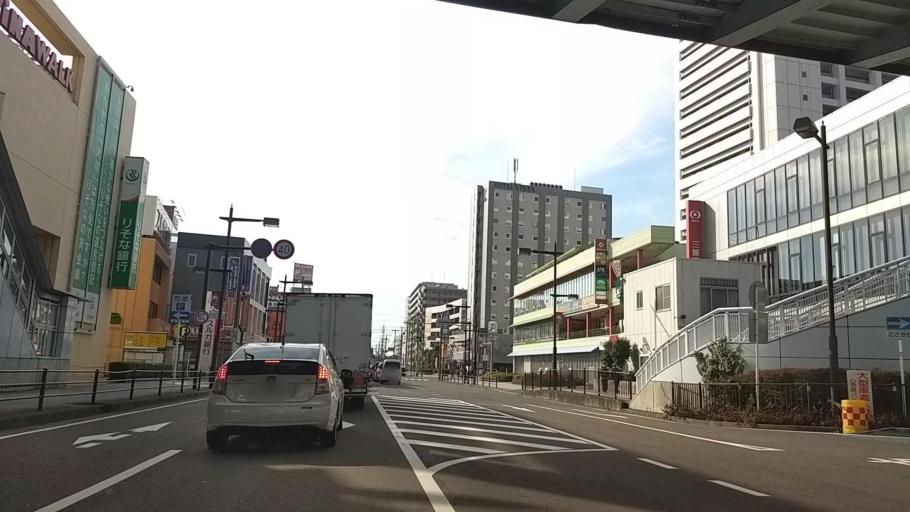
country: JP
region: Kanagawa
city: Atsugi
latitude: 35.4523
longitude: 139.3924
